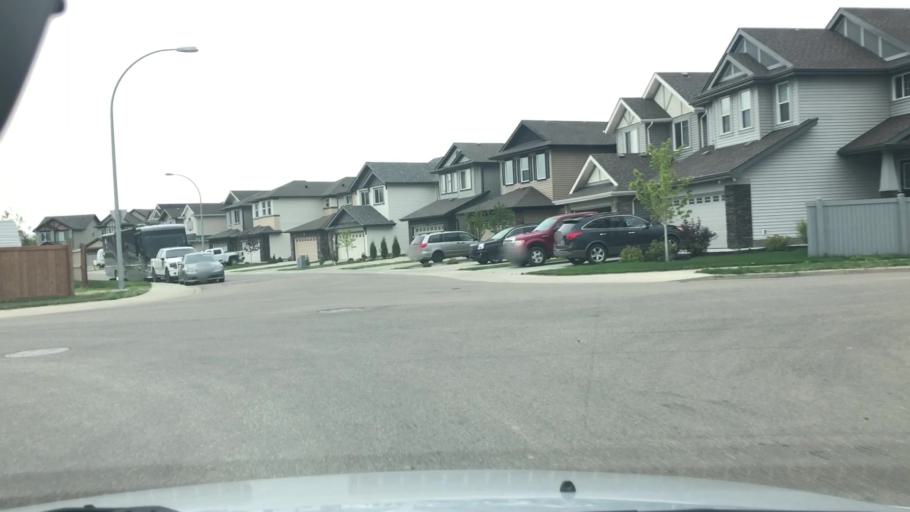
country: CA
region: Alberta
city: St. Albert
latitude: 53.6276
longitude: -113.5597
